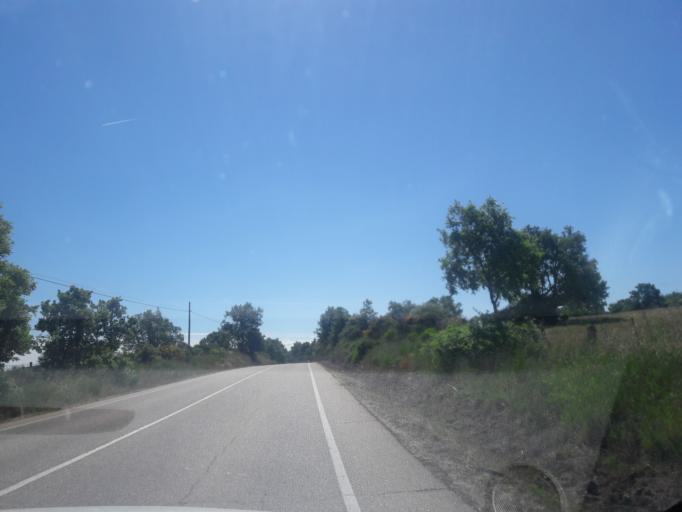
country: ES
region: Castille and Leon
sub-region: Provincia de Salamanca
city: Encinasola de los Comendadores
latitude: 40.9945
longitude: -6.5488
